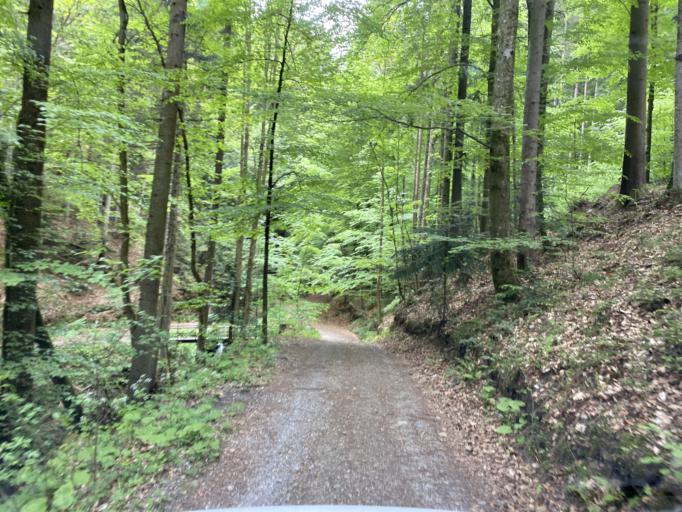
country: AT
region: Styria
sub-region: Politischer Bezirk Weiz
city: Baierdorf-Umgebung
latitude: 47.2978
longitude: 15.7066
